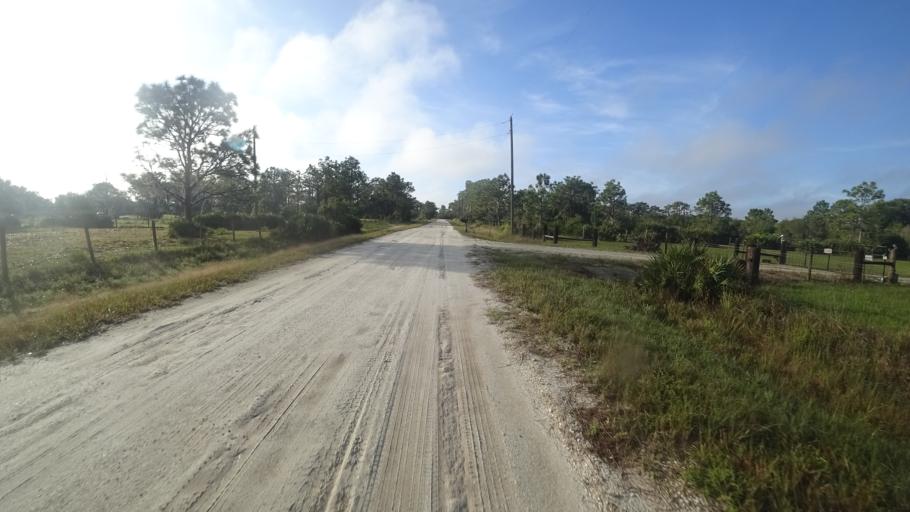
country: US
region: Florida
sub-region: Sarasota County
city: The Meadows
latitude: 27.4074
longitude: -82.2916
